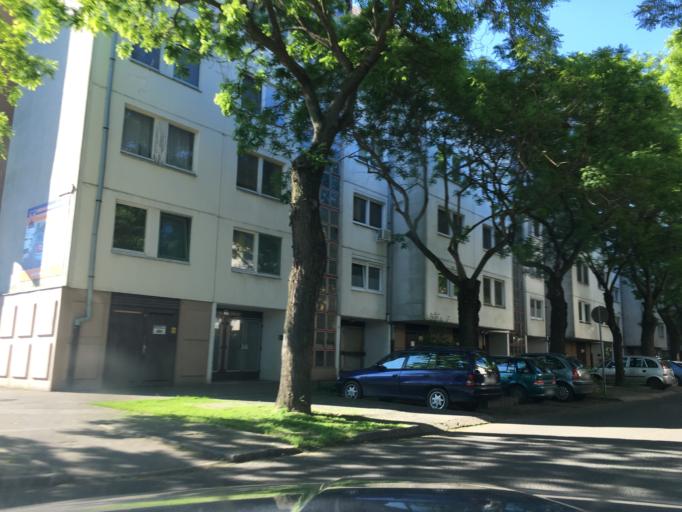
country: HU
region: Hajdu-Bihar
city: Debrecen
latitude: 47.5262
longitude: 21.6342
